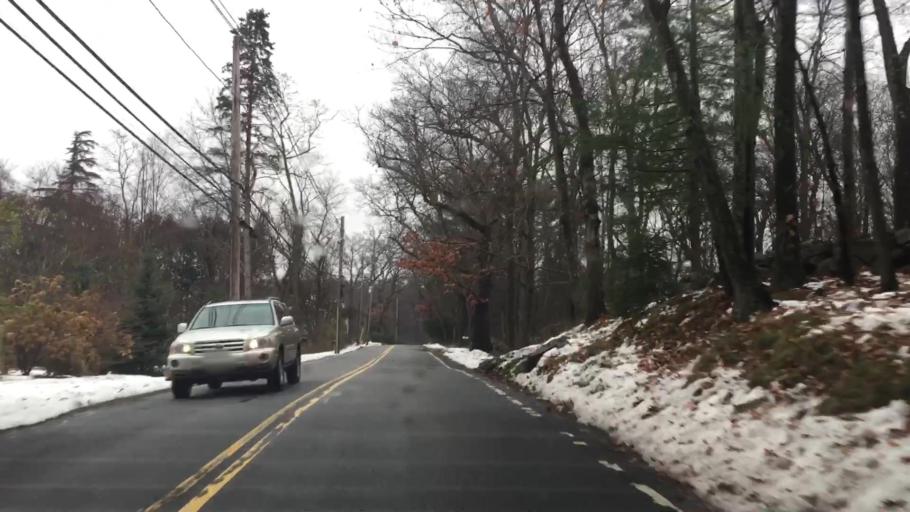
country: US
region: Massachusetts
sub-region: Essex County
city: North Andover
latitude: 42.6971
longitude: -71.0837
